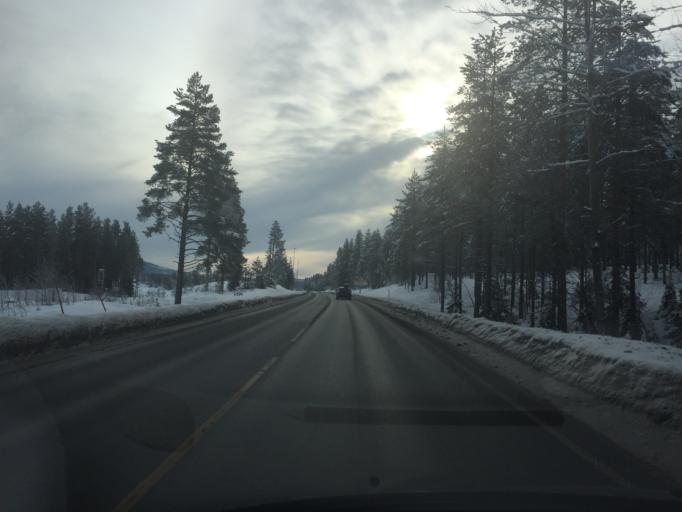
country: NO
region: Hedmark
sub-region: Trysil
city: Innbygda
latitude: 61.3006
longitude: 12.2626
